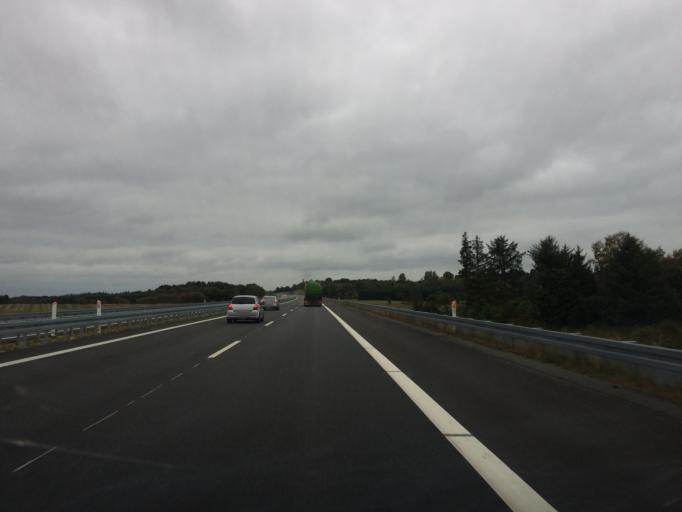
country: DK
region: Central Jutland
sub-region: Silkeborg Kommune
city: Silkeborg
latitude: 56.1866
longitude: 9.4902
